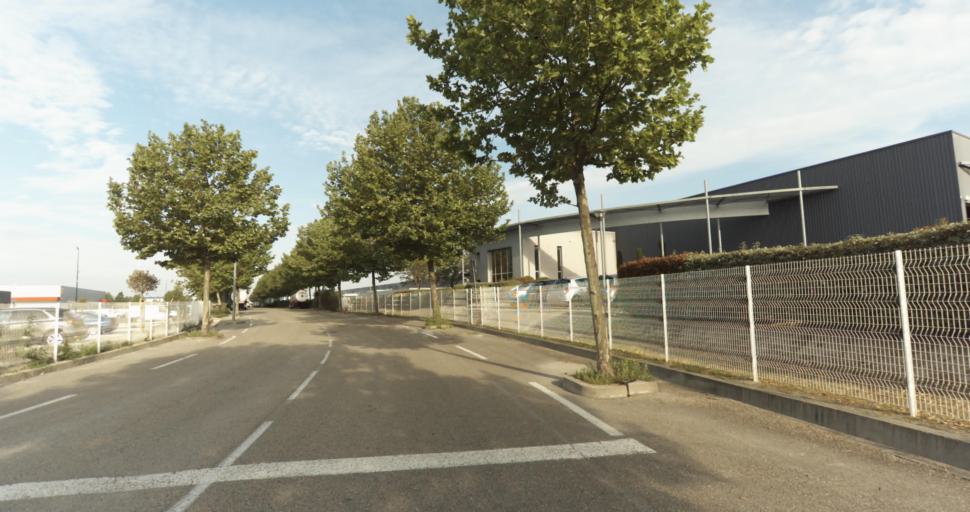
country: FR
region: Languedoc-Roussillon
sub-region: Departement du Gard
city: Rodilhan
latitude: 43.8398
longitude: 4.4280
